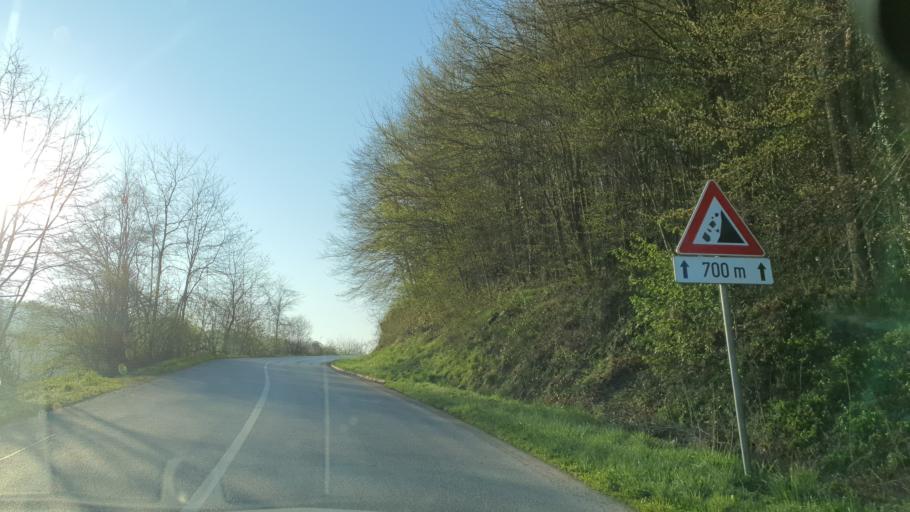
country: RS
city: Jarebice
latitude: 44.4778
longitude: 19.4824
